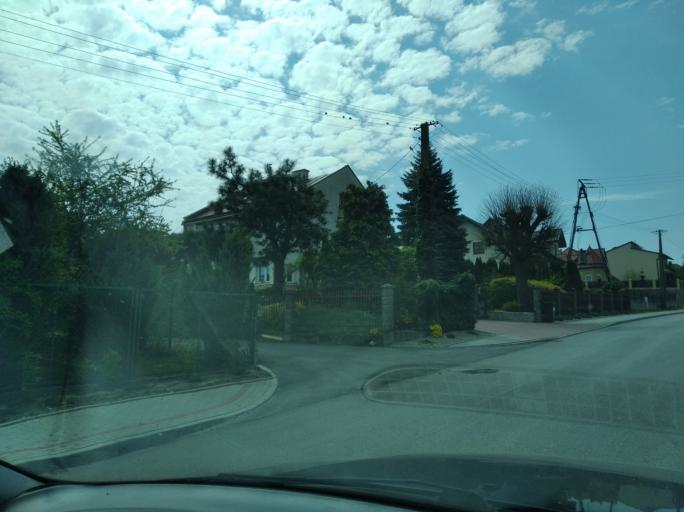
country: PL
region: Subcarpathian Voivodeship
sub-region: Powiat jaroslawski
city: Jaroslaw
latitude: 50.0049
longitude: 22.6817
